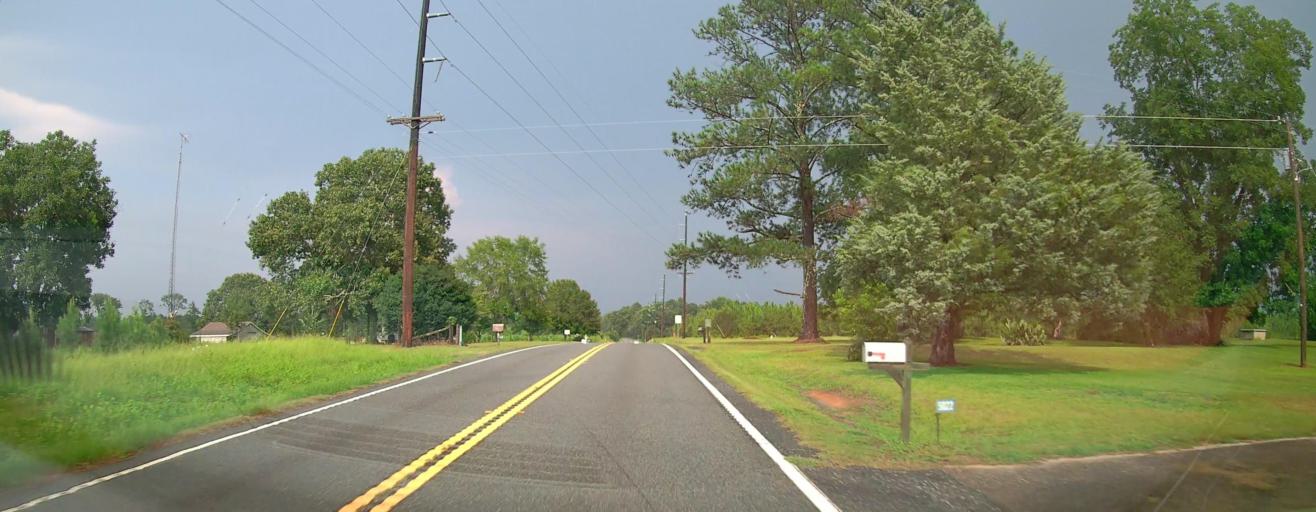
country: US
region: Georgia
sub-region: Twiggs County
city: Jeffersonville
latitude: 32.6041
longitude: -83.2924
